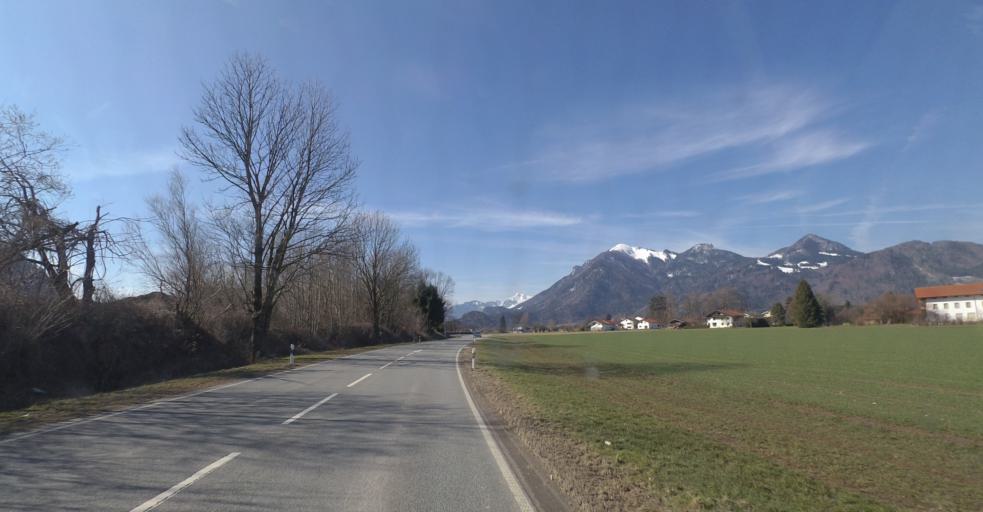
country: DE
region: Bavaria
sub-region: Upper Bavaria
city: Staudach-Egerndach
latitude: 47.7752
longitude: 12.4742
